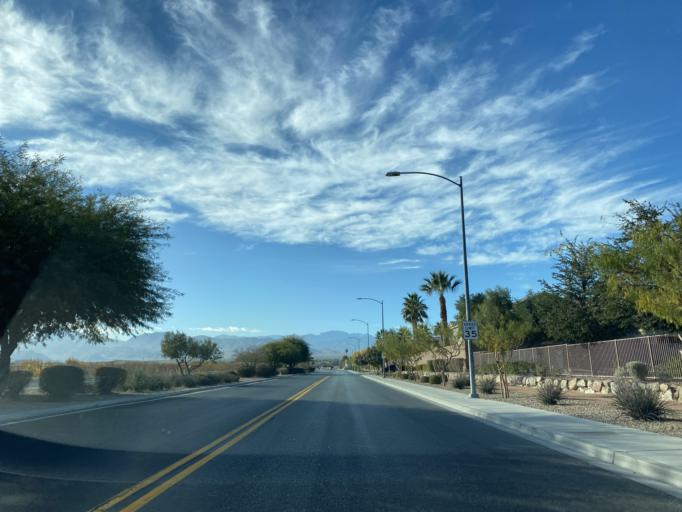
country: US
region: Nevada
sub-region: Clark County
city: North Las Vegas
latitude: 36.3053
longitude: -115.2476
